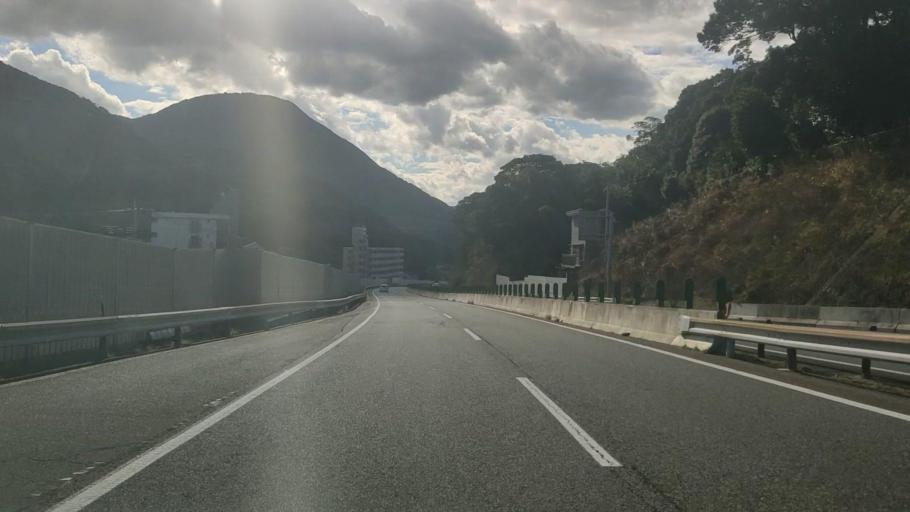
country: JP
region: Yamaguchi
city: Shimonoseki
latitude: 33.9151
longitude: 130.9616
